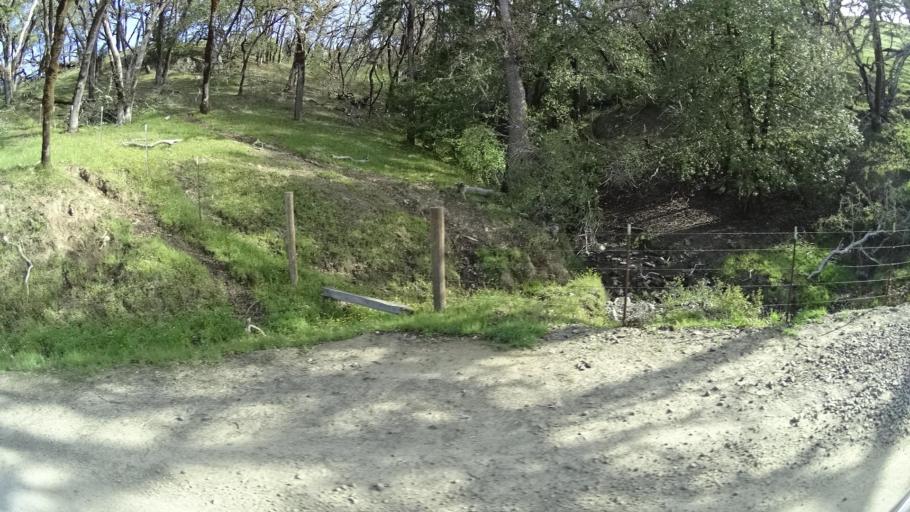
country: US
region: California
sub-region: Humboldt County
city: Hydesville
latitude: 40.6410
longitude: -123.8890
